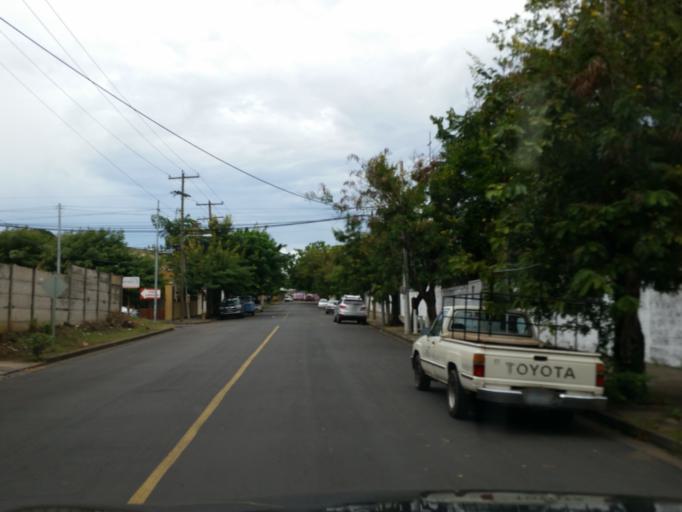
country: NI
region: Managua
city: Managua
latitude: 12.1406
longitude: -86.2807
